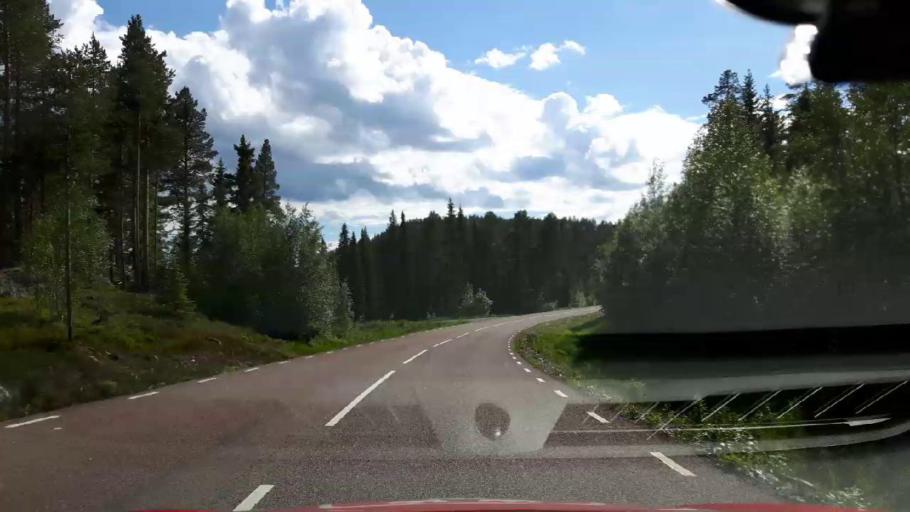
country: SE
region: Jaemtland
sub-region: Krokoms Kommun
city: Valla
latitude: 64.0008
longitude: 14.2385
